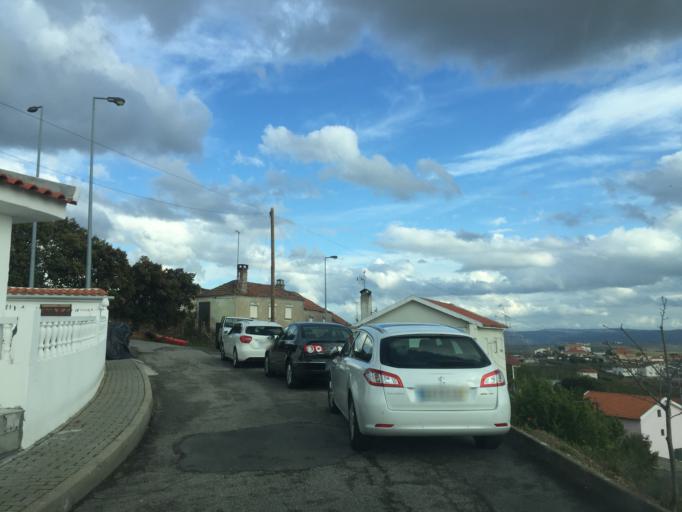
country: PT
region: Braganca
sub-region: Alfandega da Fe
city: Alfandega da Fe
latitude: 41.3402
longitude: -6.9662
